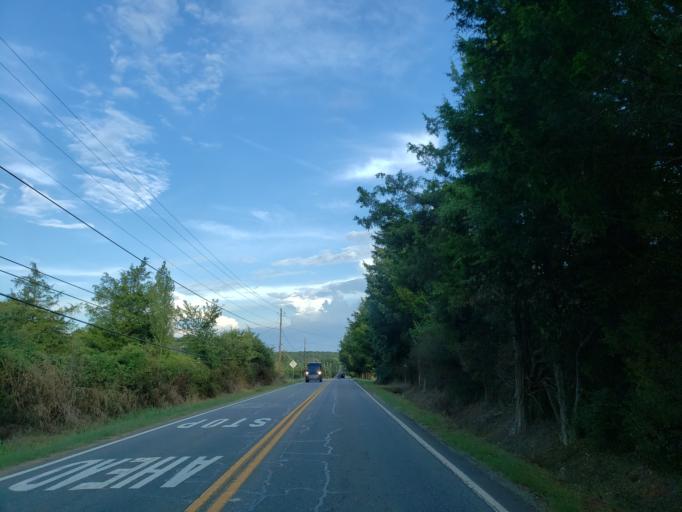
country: US
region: Georgia
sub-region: Bartow County
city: Cartersville
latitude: 34.2324
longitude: -84.8641
